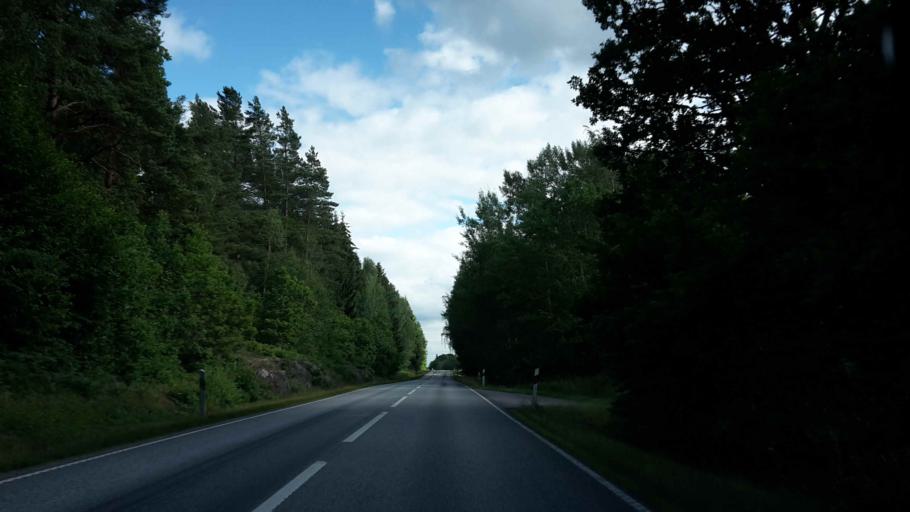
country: SE
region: OEstergoetland
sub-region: Linkopings Kommun
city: Ljungsbro
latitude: 58.7718
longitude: 15.5153
